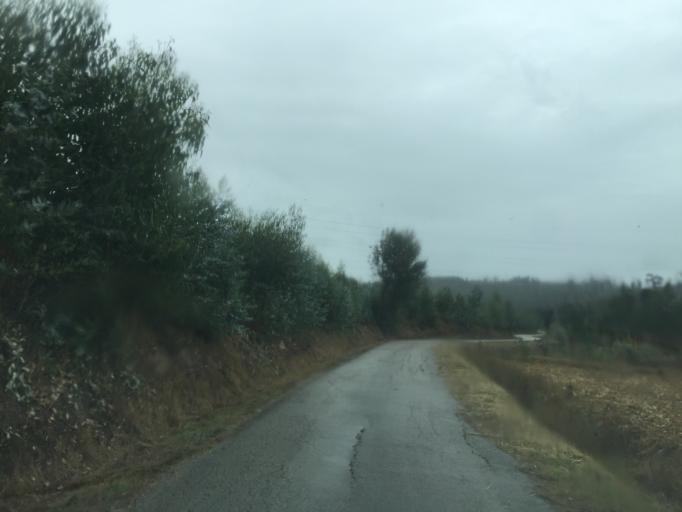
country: PT
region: Coimbra
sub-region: Figueira da Foz
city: Lavos
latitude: 40.0835
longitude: -8.7997
